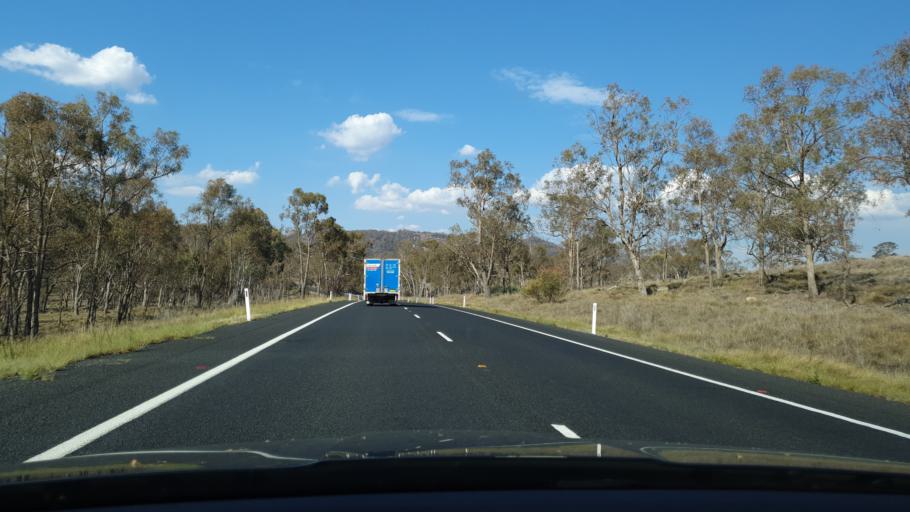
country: AU
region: New South Wales
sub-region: Glen Innes Severn
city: Glen Innes
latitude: -29.3697
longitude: 151.8957
